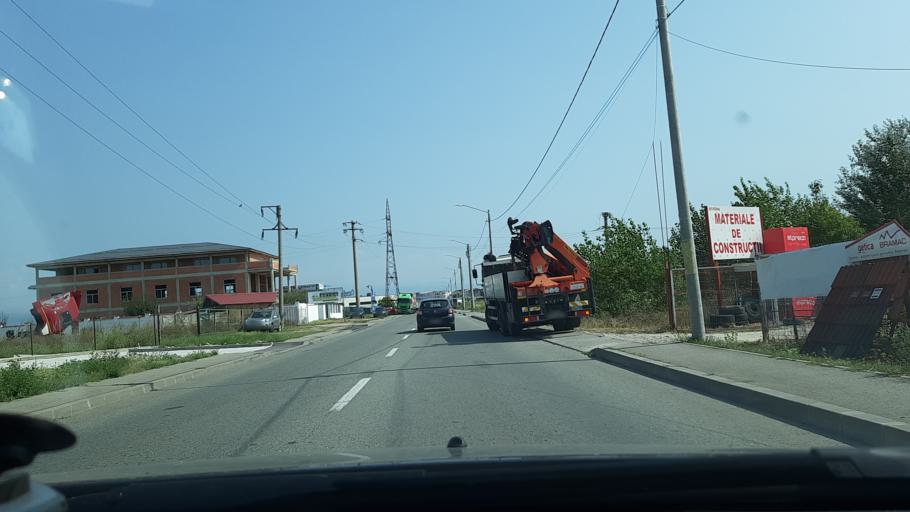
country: RO
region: Gorj
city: Targu Jiu
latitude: 45.0195
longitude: 23.2614
